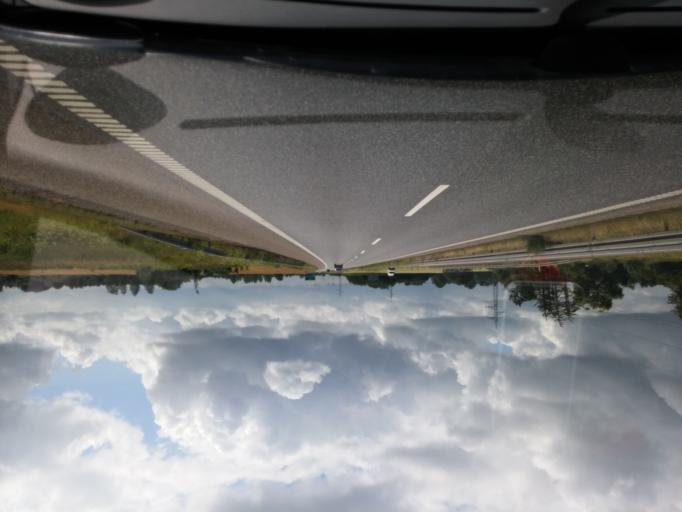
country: DK
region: South Denmark
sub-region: Faaborg-Midtfyn Kommune
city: Ringe
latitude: 55.1838
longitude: 10.5321
